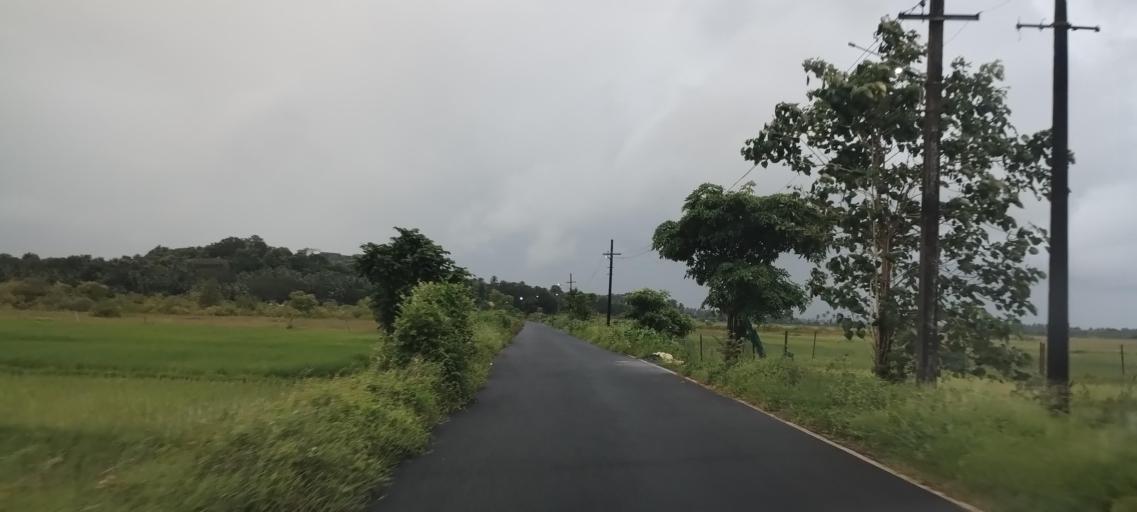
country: IN
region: Goa
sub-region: North Goa
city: Serula
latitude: 15.5169
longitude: 73.8931
